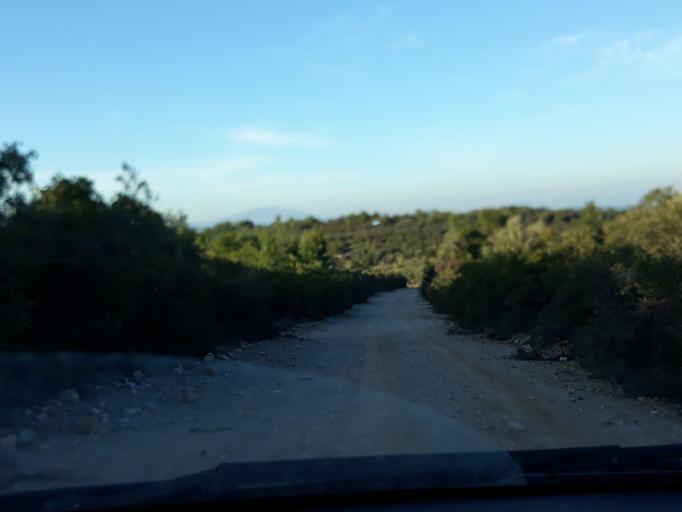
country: GR
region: Central Greece
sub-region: Nomos Voiotias
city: Asopia
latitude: 38.2530
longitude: 23.5312
